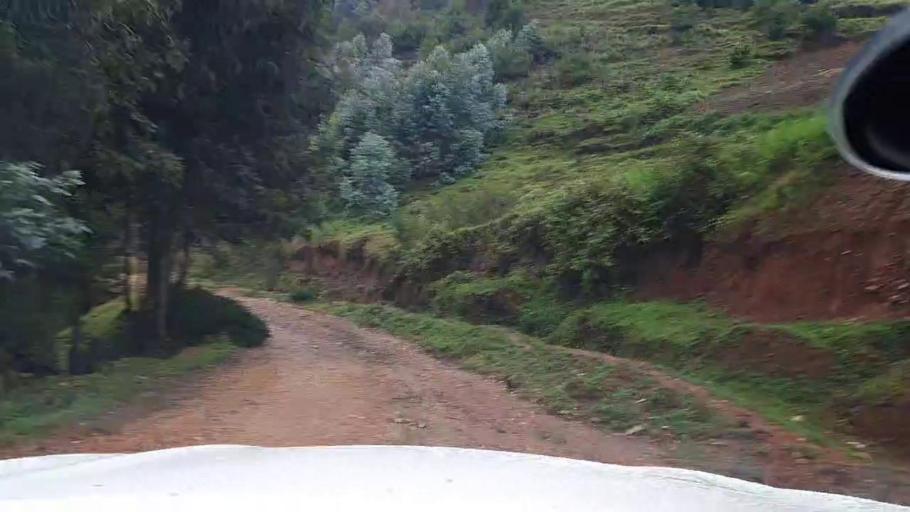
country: RW
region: Western Province
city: Kibuye
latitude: -2.1375
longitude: 29.4586
